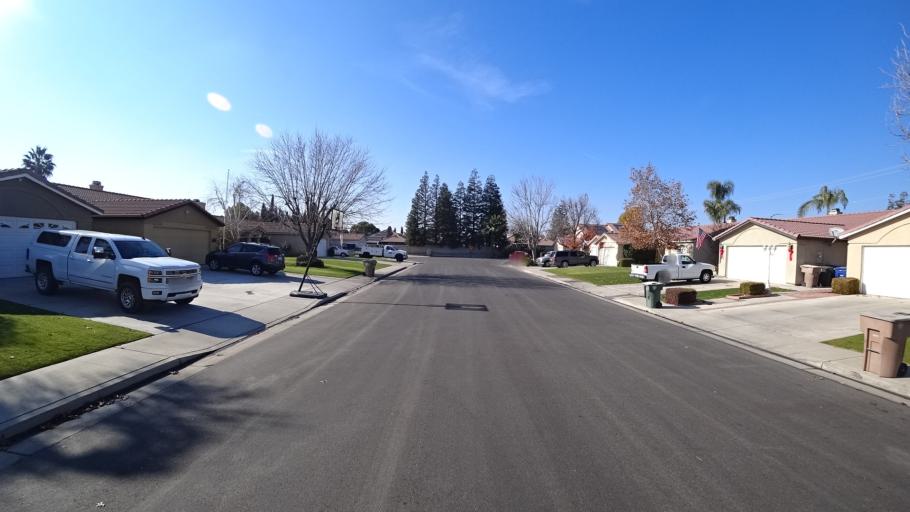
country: US
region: California
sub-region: Kern County
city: Greenacres
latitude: 35.3247
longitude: -119.1223
